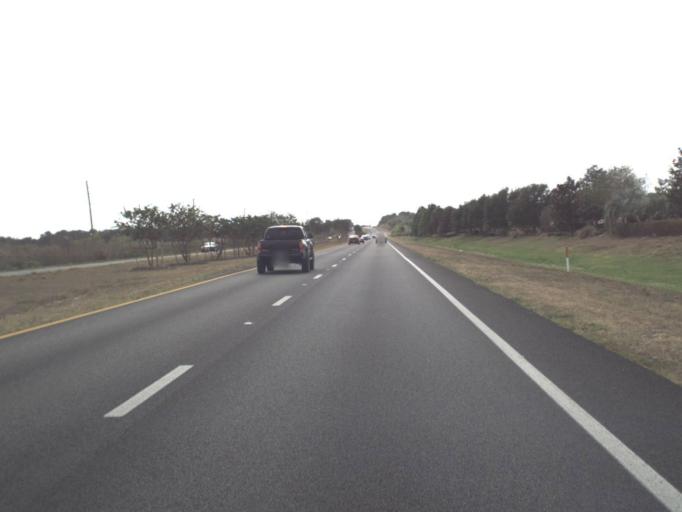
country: US
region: Florida
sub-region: Lake County
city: Clermont
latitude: 28.5584
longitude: -81.7961
